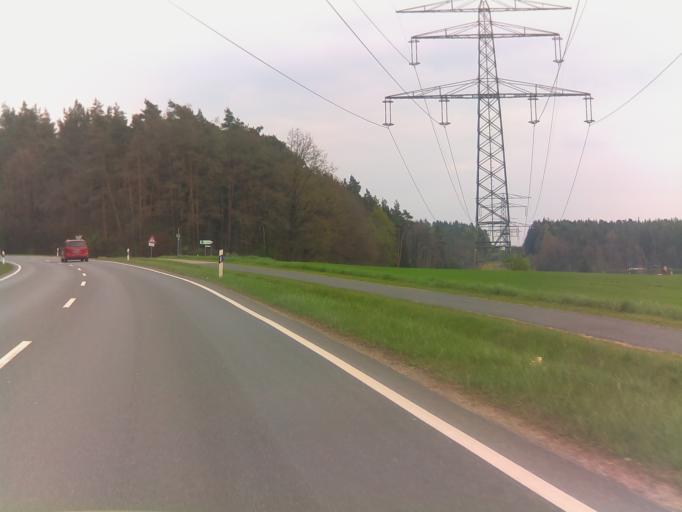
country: DE
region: Bavaria
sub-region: Regierungsbezirk Mittelfranken
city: Schnaittach
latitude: 49.5682
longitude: 11.3161
